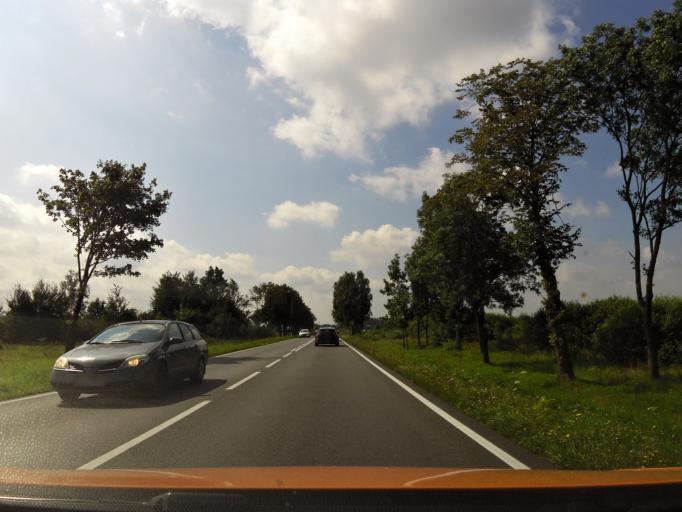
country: PL
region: West Pomeranian Voivodeship
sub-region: Powiat goleniowski
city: Nowogard
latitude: 53.7283
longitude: 15.1998
